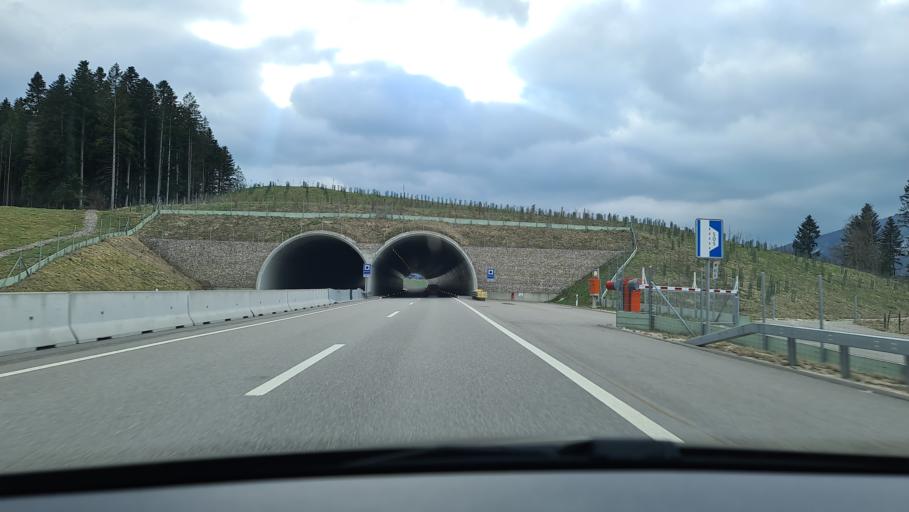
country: CH
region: Bern
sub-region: Jura bernois
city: Bevilard
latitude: 47.2306
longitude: 7.2796
